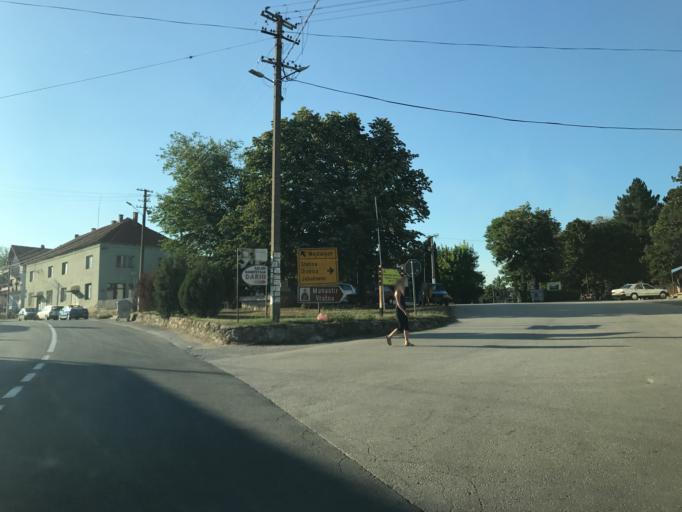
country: RO
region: Mehedinti
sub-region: Comuna Gogosu
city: Ostrovu Mare
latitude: 44.2905
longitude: 22.3531
